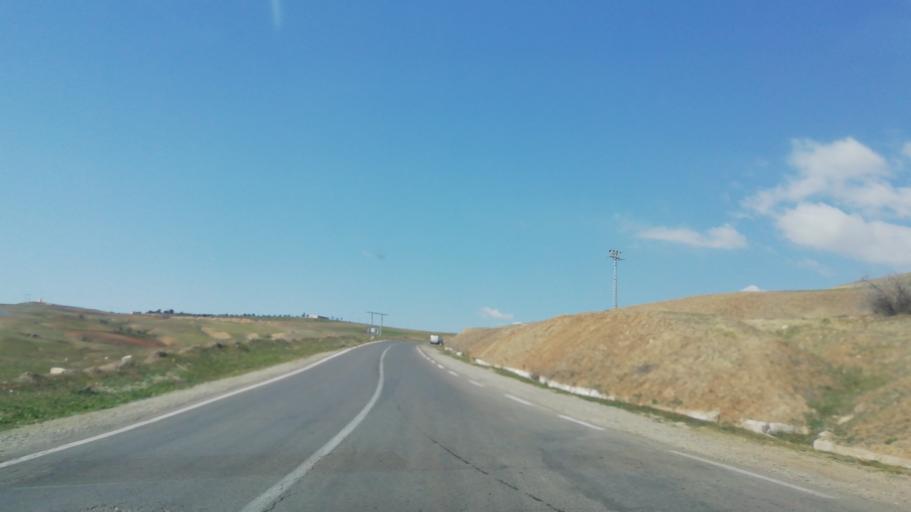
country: DZ
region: Mascara
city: Mascara
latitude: 35.5399
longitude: 0.1130
